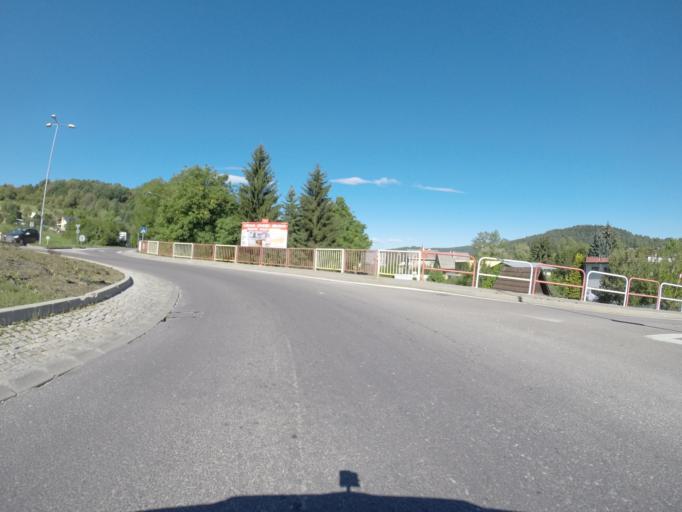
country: SK
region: Trenciansky
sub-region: Okres Povazska Bystrica
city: Povazska Bystrica
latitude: 49.1025
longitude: 18.4571
